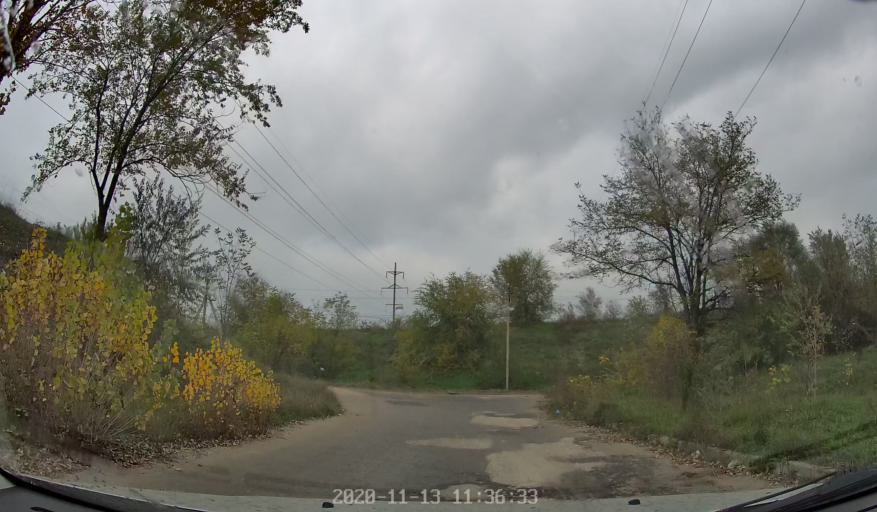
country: MD
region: Chisinau
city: Chisinau
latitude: 46.9889
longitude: 28.9160
